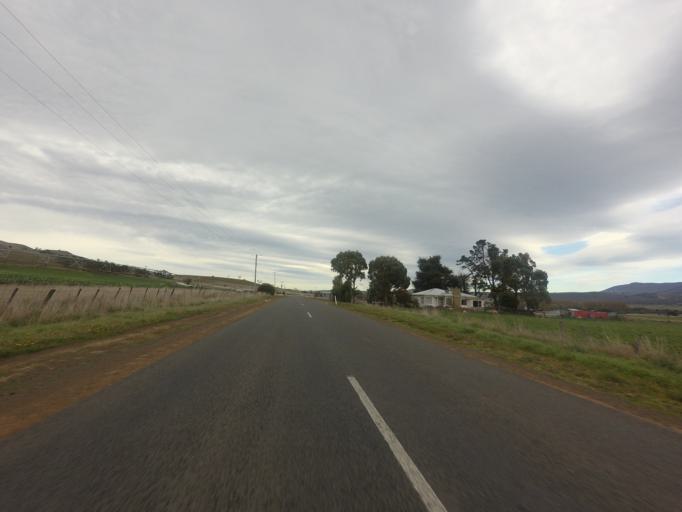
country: AU
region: Tasmania
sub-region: Derwent Valley
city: New Norfolk
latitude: -42.5017
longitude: 146.7344
